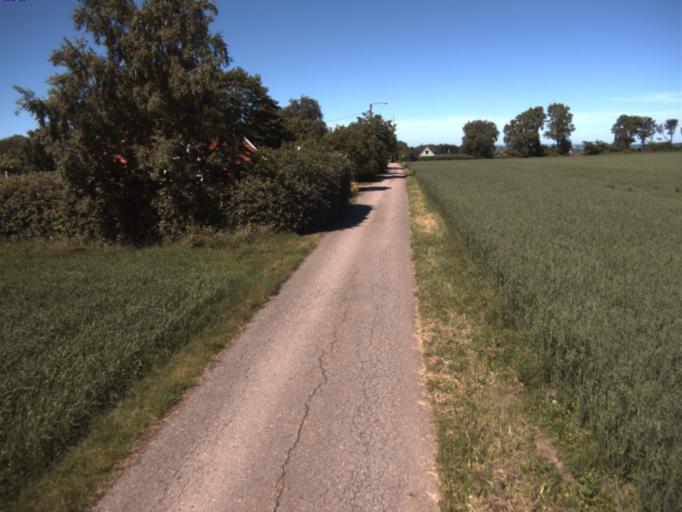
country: SE
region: Skane
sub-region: Helsingborg
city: Morarp
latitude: 56.0631
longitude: 12.8796
